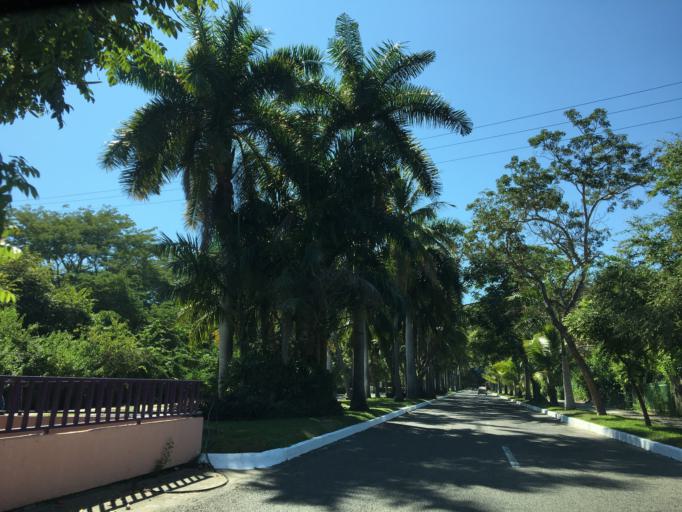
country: MX
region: Oaxaca
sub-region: Santa Maria Huatulco
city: Crucecita
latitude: 15.7752
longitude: -96.1011
